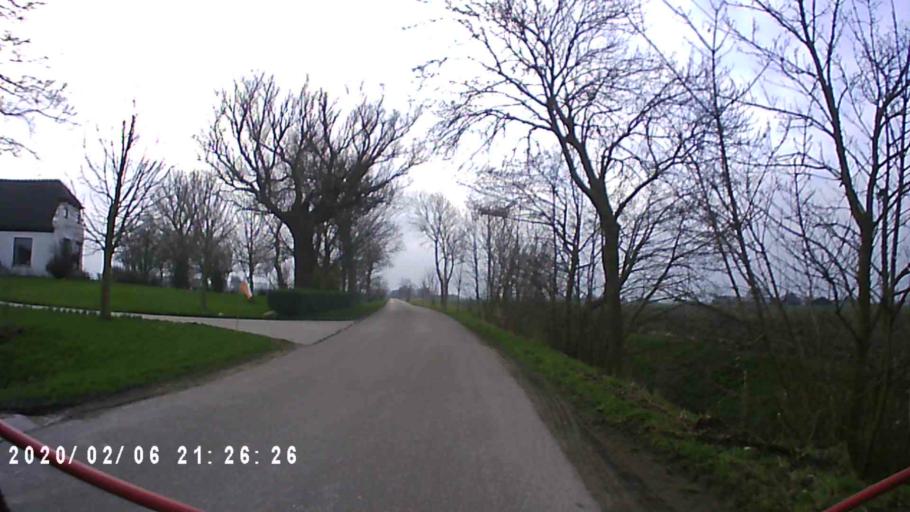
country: NL
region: Groningen
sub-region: Gemeente Zuidhorn
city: Oldehove
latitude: 53.2878
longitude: 6.3777
